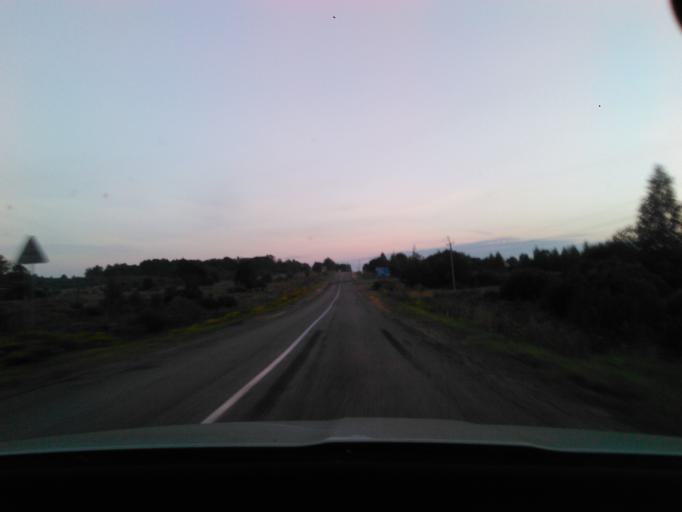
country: RU
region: Moskovskaya
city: Klin
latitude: 56.2187
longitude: 36.7327
